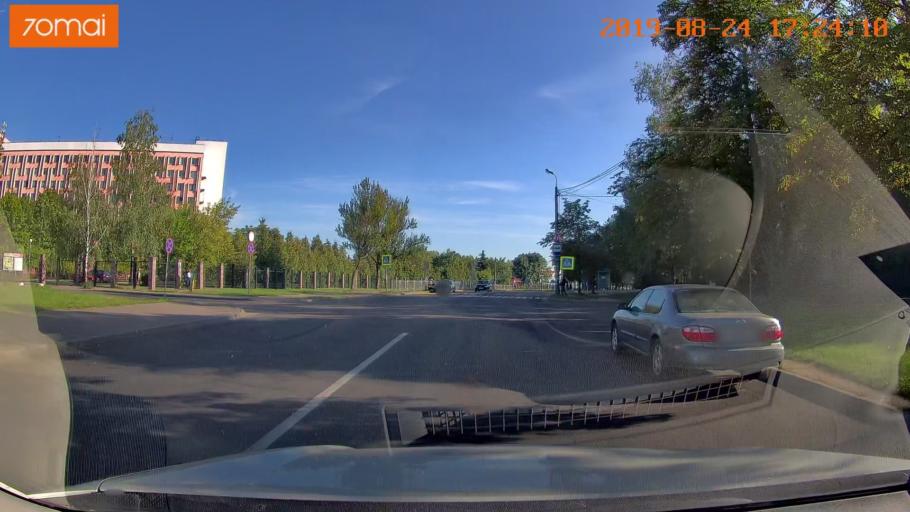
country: BY
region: Minsk
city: Hatava
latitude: 53.8390
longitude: 27.6530
